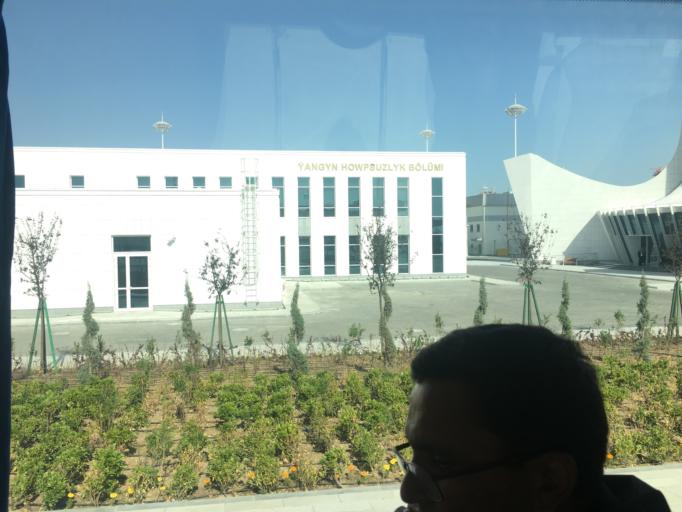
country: TM
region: Balkan
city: Turkmenbasy
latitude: 40.0044
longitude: 53.0223
